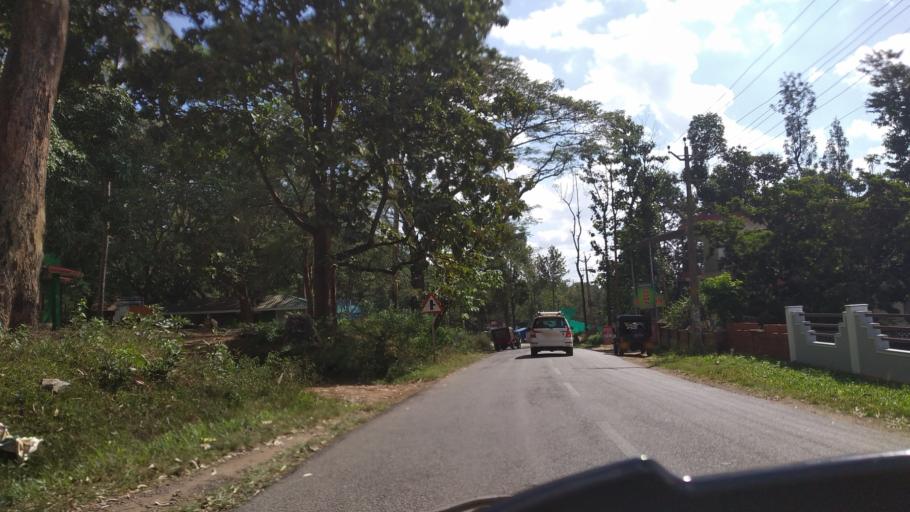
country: IN
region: Kerala
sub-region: Wayanad
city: Panamaram
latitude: 11.9452
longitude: 76.0647
